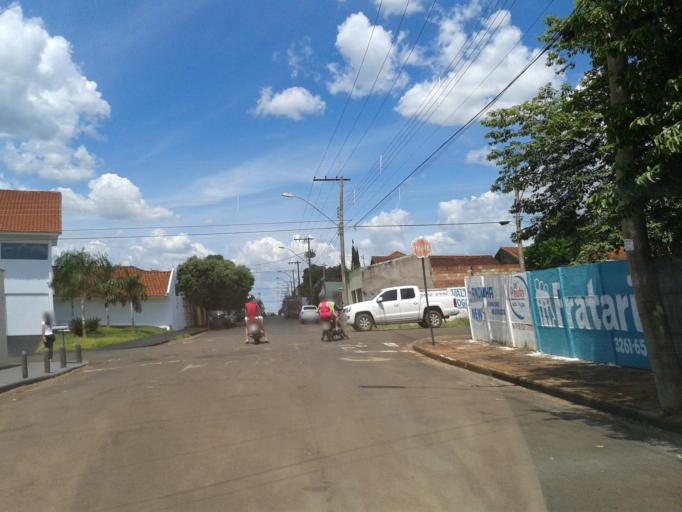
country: BR
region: Minas Gerais
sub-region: Ituiutaba
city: Ituiutaba
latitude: -18.9815
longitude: -49.4607
